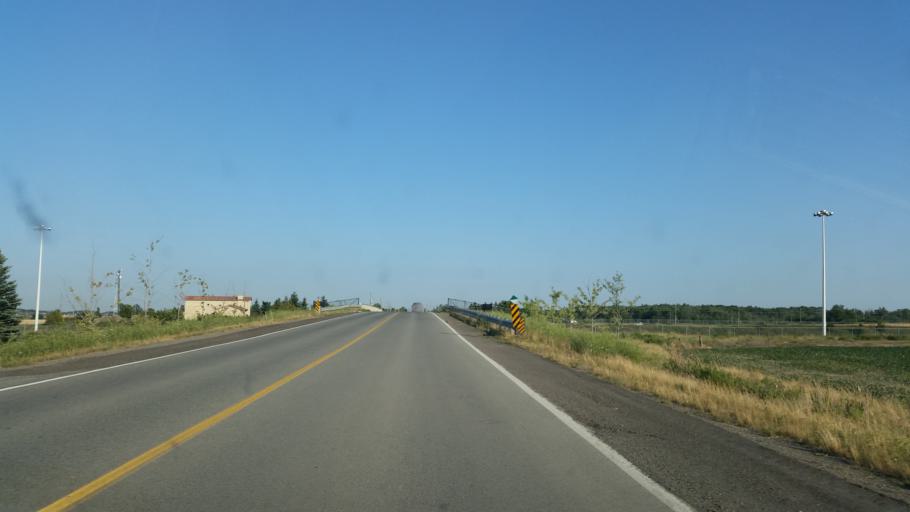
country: CA
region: Ontario
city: Brampton
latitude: 43.7564
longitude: -79.8082
